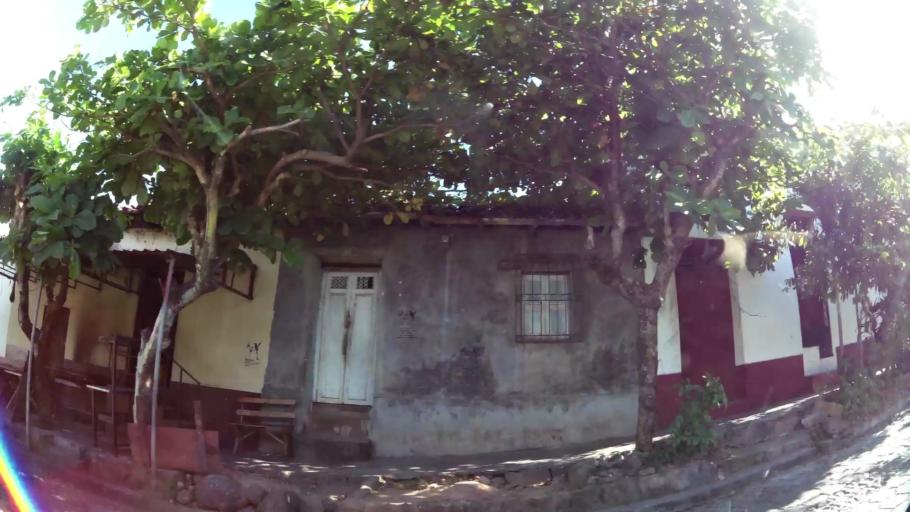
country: SV
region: Cuscatlan
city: Suchitoto
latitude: 13.9383
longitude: -89.0251
